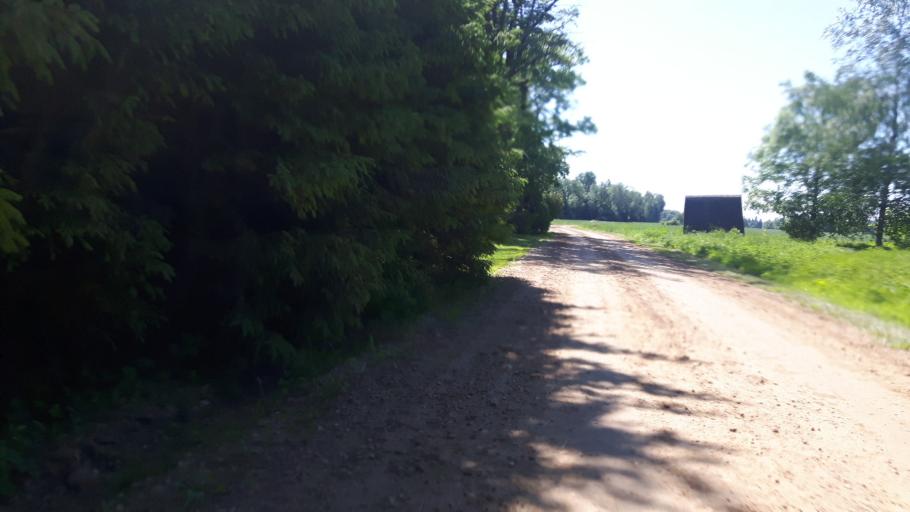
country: EE
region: Paernumaa
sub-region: Tootsi vald
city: Tootsi
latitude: 58.5034
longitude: 24.9065
